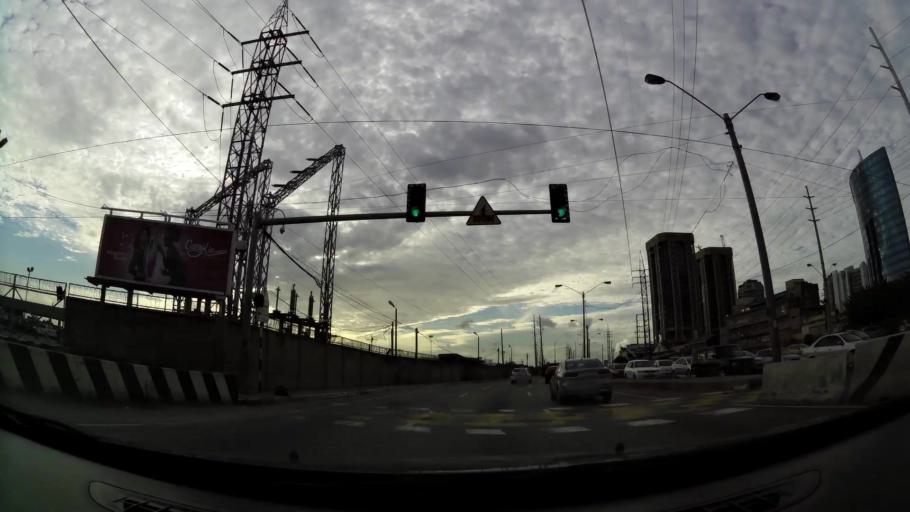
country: TT
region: San Juan/Laventille
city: Laventille
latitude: 10.6474
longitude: -61.5096
